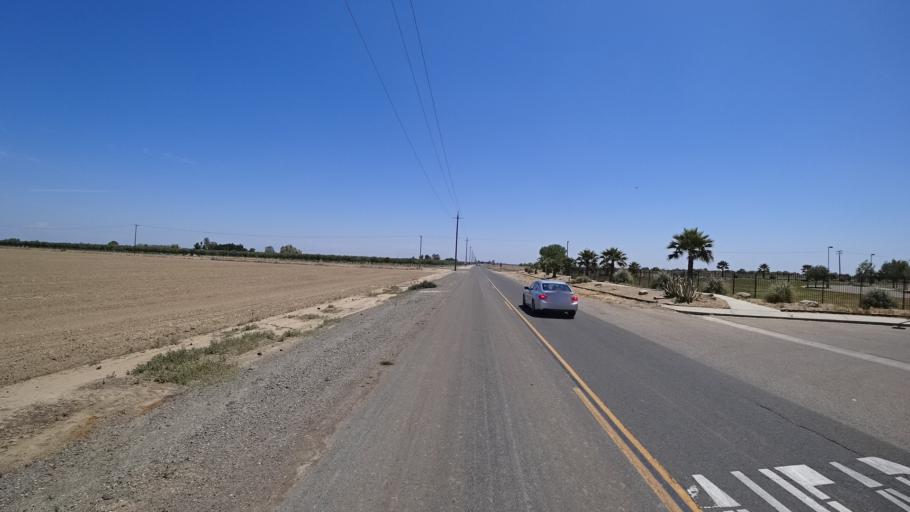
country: US
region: California
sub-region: Kings County
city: Lemoore
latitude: 36.2403
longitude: -119.7458
